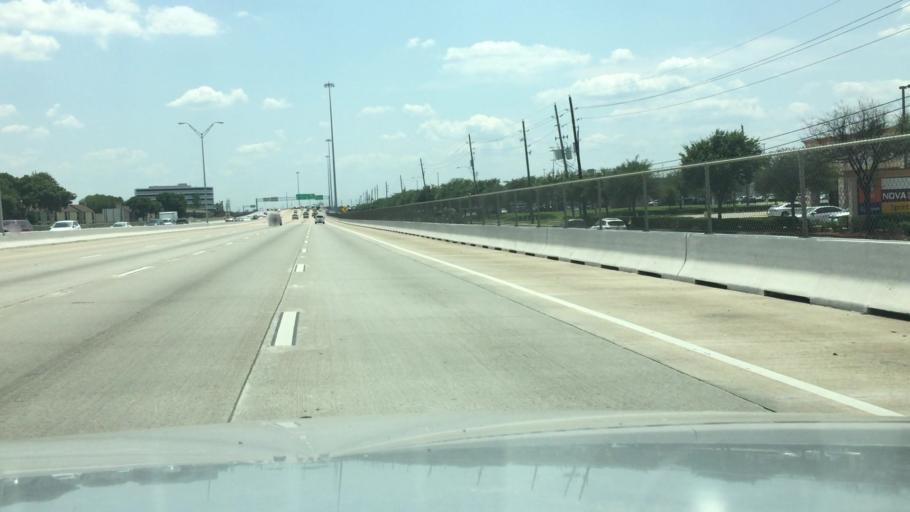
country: US
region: Texas
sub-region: Fort Bend County
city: Meadows Place
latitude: 29.6821
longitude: -95.5591
